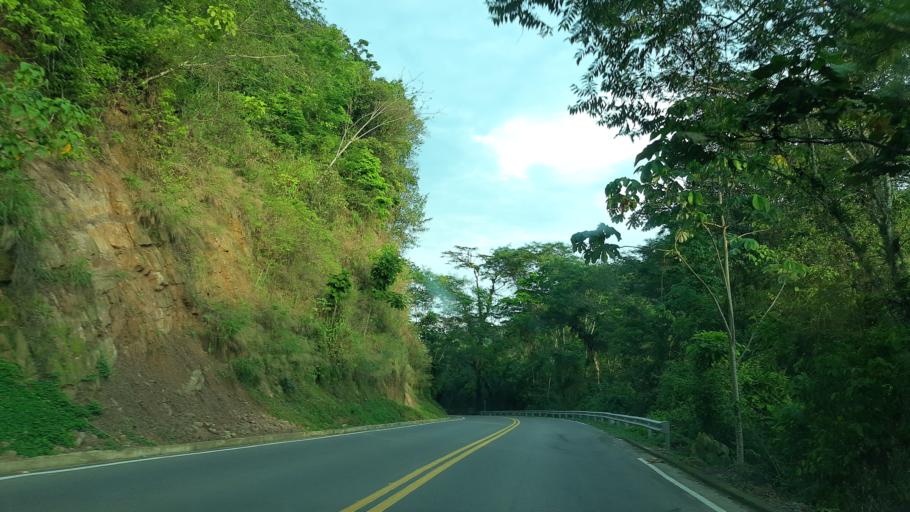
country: CO
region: Boyaca
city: San Luis de Gaceno
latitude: 4.8311
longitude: -73.1181
